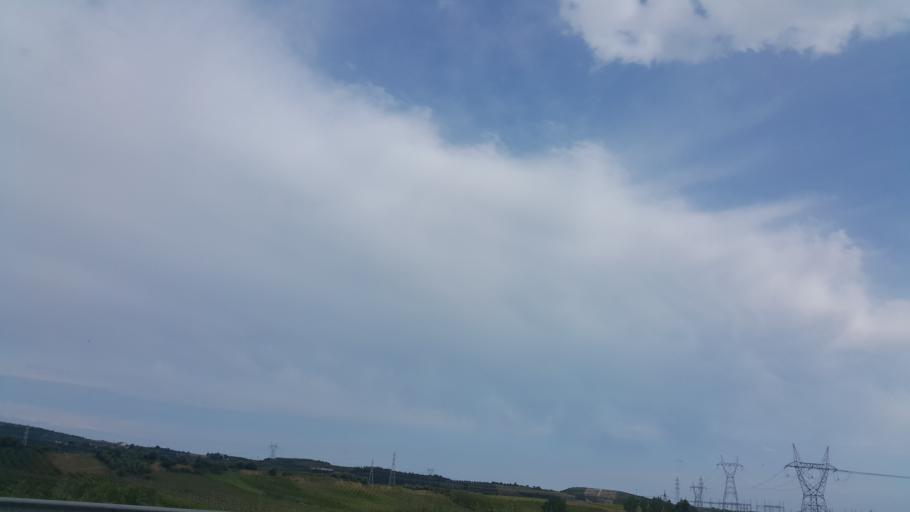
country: TR
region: Mersin
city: Kazanli
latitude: 36.9228
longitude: 34.6984
